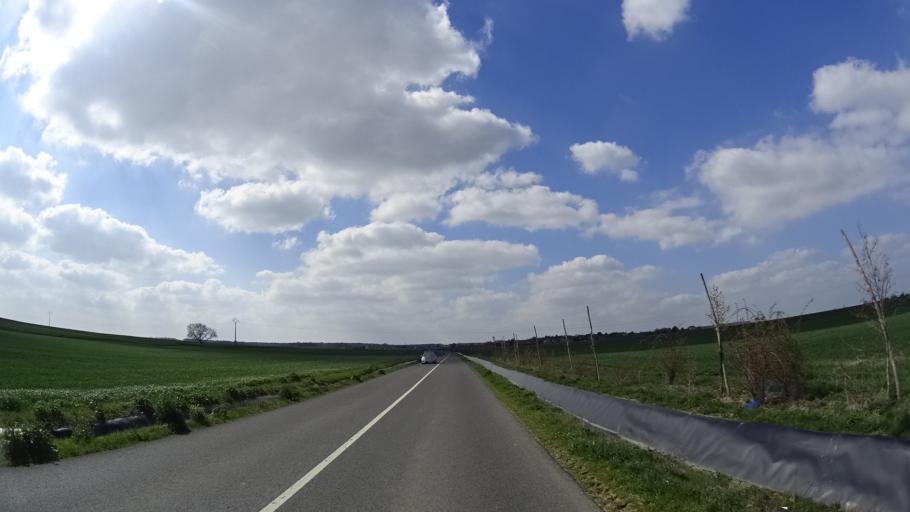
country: FR
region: Pays de la Loire
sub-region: Departement de Maine-et-Loire
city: Breze
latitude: 47.0810
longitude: -0.0153
